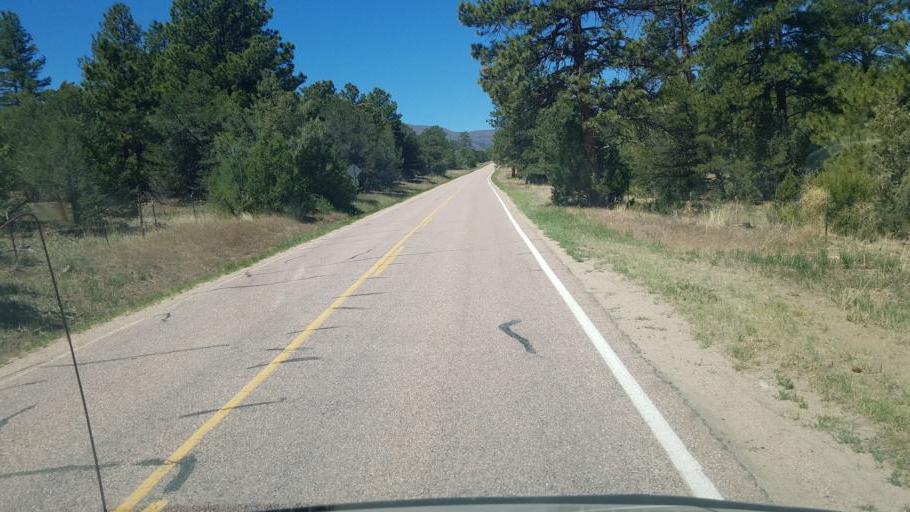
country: US
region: Colorado
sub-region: Custer County
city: Westcliffe
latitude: 38.3105
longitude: -105.6275
